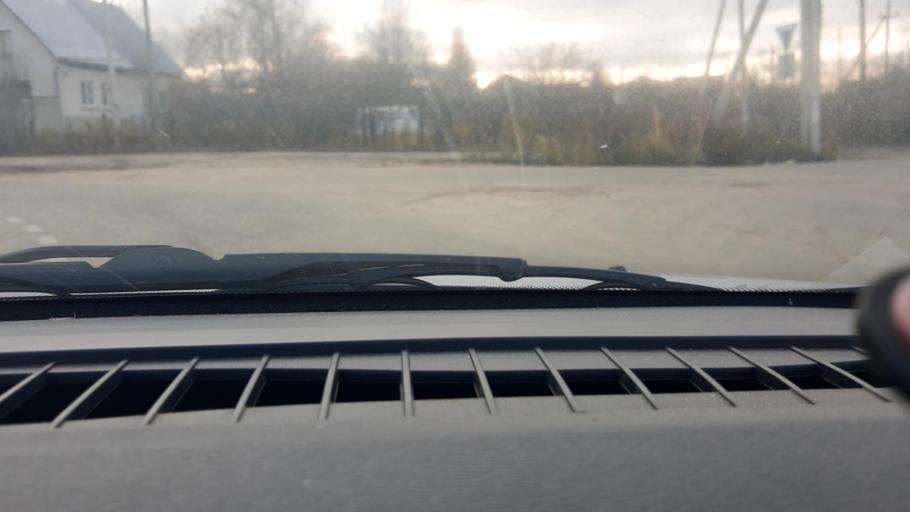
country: RU
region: Nizjnij Novgorod
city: Afonino
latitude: 56.2739
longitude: 44.0416
